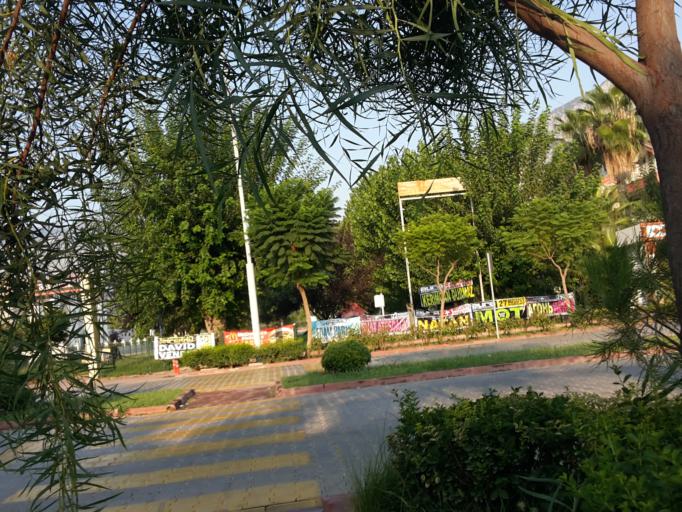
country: TR
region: Antalya
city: Kemer
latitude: 36.6061
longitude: 30.5589
